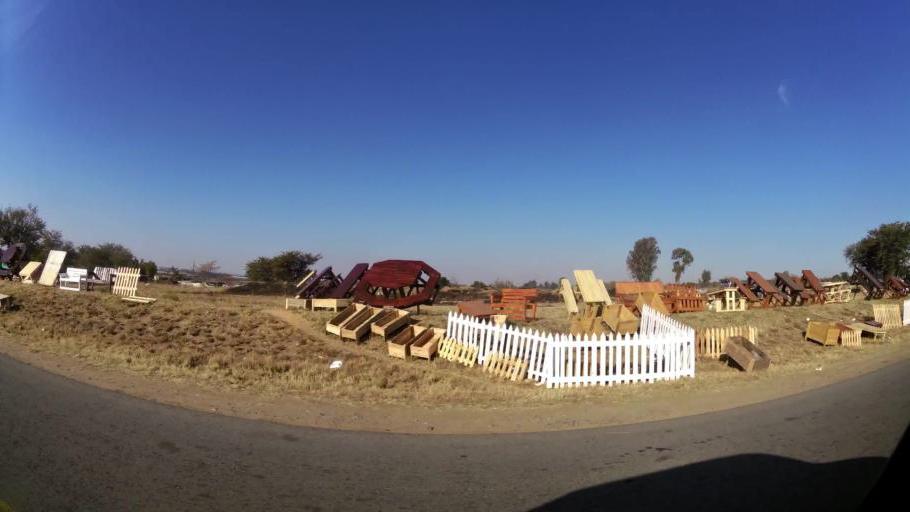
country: ZA
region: Gauteng
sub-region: West Rand District Municipality
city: Muldersdriseloop
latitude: -25.9868
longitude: 27.9250
